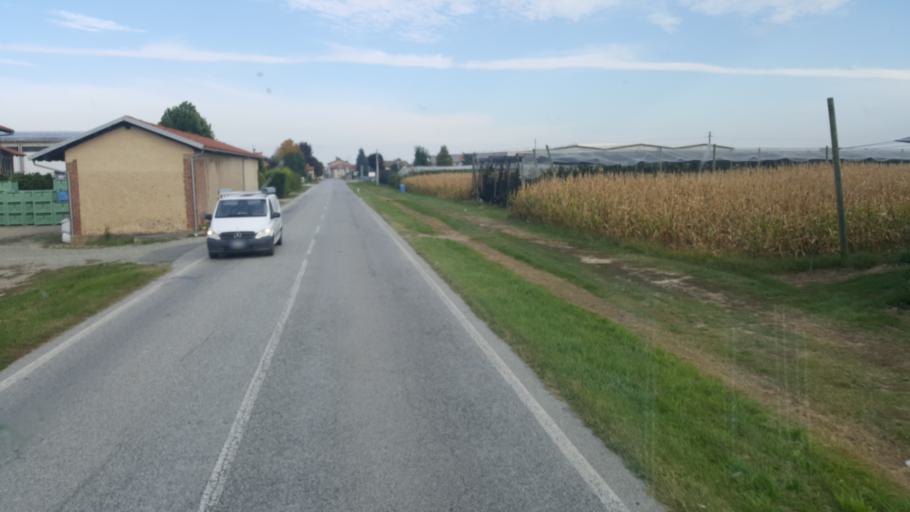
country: IT
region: Piedmont
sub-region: Provincia di Cuneo
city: Verzuolo
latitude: 44.5976
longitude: 7.5048
